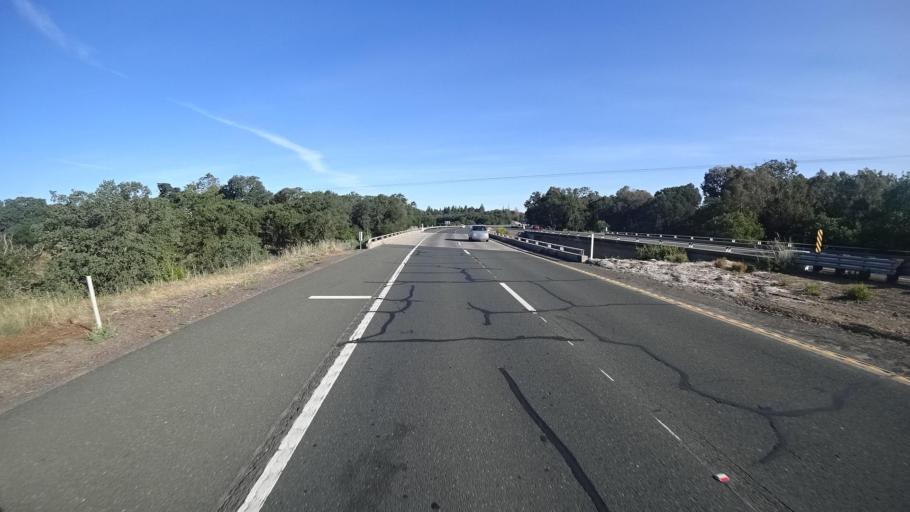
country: US
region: California
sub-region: Lake County
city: Lakeport
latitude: 39.0401
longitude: -122.9299
